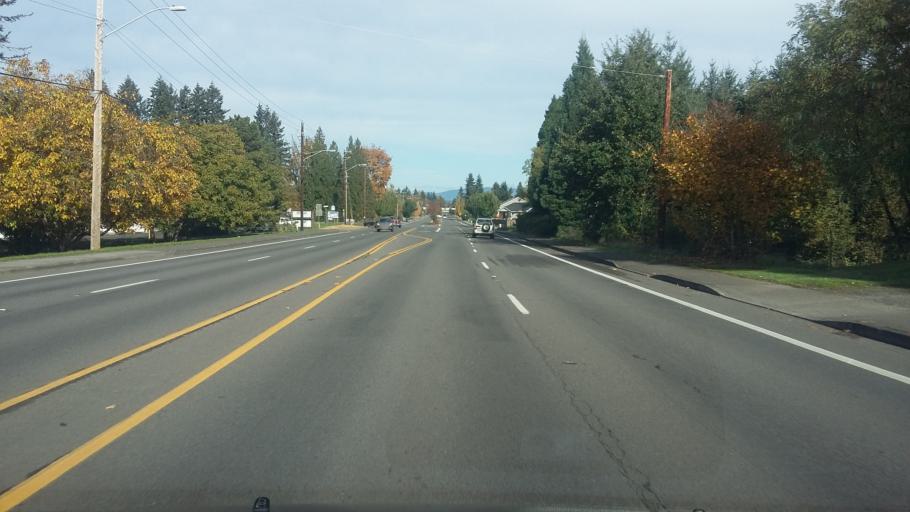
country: US
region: Washington
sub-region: Clark County
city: Barberton
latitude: 45.6888
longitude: -122.6217
